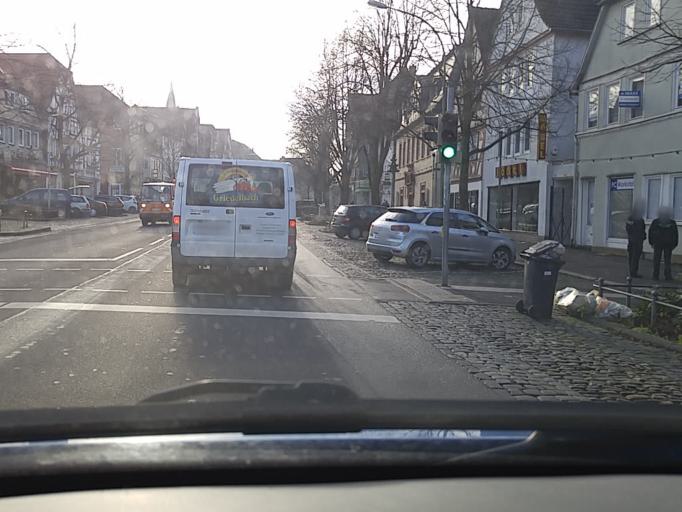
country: DE
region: Hesse
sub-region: Regierungsbezirk Darmstadt
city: Friedberg
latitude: 50.3397
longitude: 8.7541
